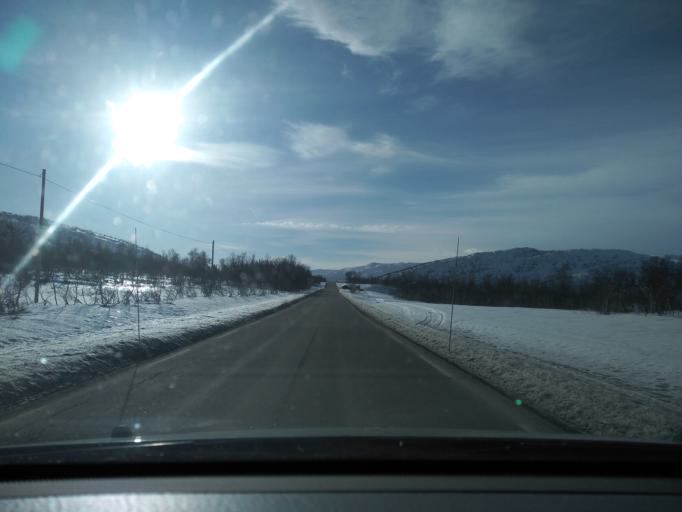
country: NO
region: Aust-Agder
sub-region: Bykle
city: Hovden
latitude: 59.6492
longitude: 7.4722
